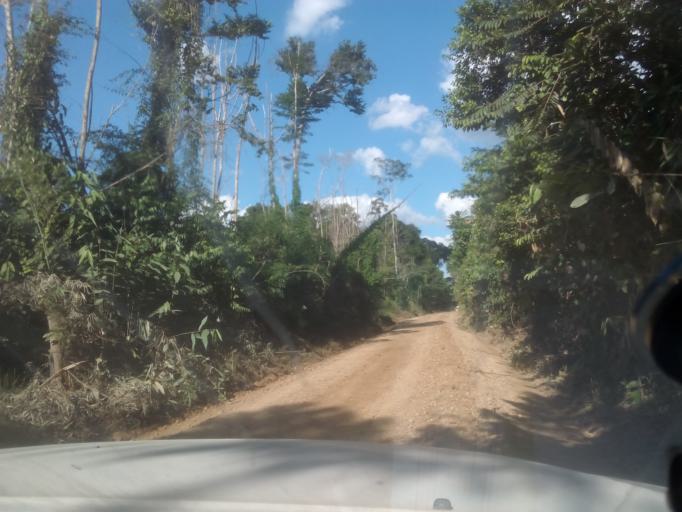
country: PE
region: Cusco
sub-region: Provincia de Quispicanchis
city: Quince Mil
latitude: -12.6407
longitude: -70.3703
